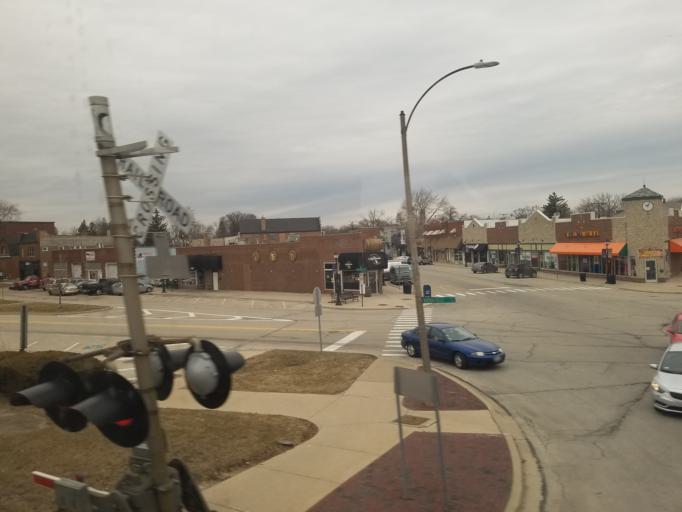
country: US
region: Illinois
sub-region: Cook County
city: Brookfield
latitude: 41.8219
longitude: -87.8438
